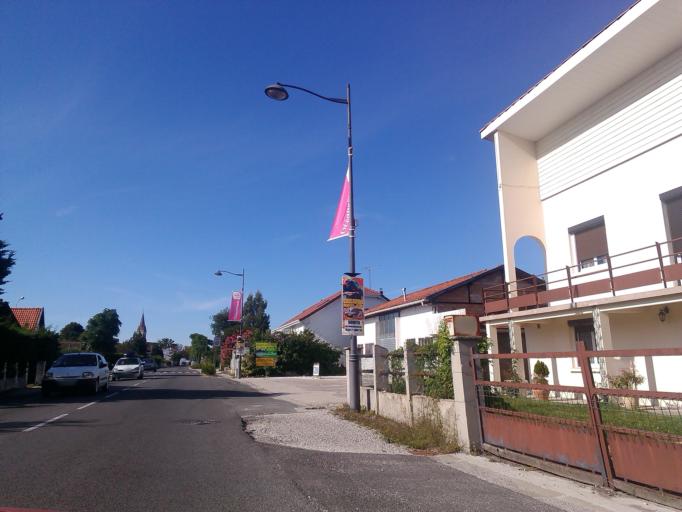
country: FR
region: Aquitaine
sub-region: Departement de la Gironde
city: Hourtin
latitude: 45.1822
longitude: -1.0562
